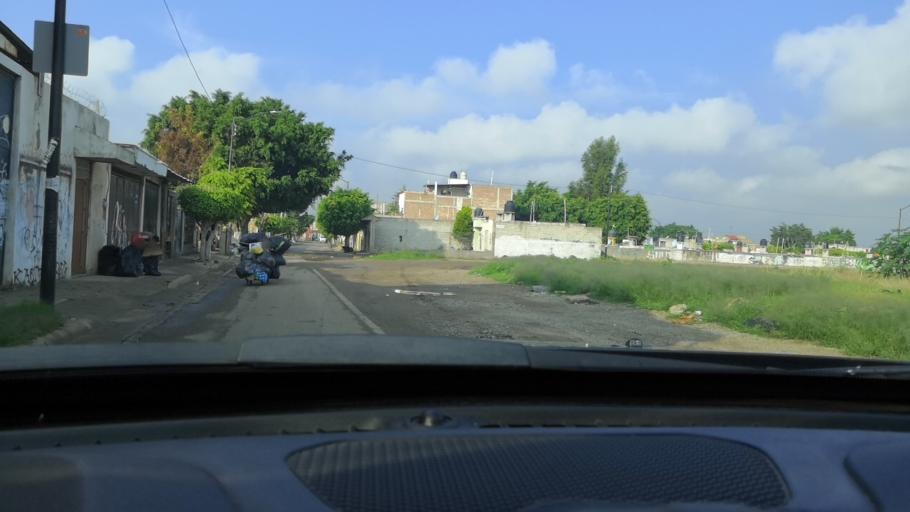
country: MX
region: Guanajuato
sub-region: Leon
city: Fraccionamiento Paraiso Real
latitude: 21.1016
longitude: -101.5882
